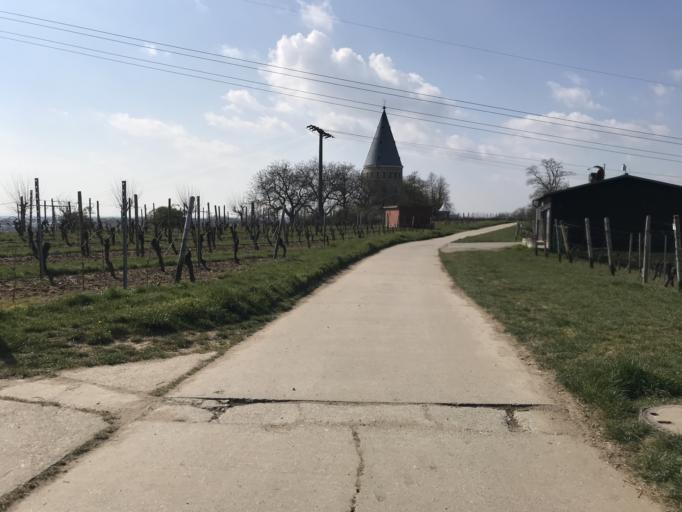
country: DE
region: Hesse
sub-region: Regierungsbezirk Darmstadt
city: Florsheim
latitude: 50.0210
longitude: 8.4044
